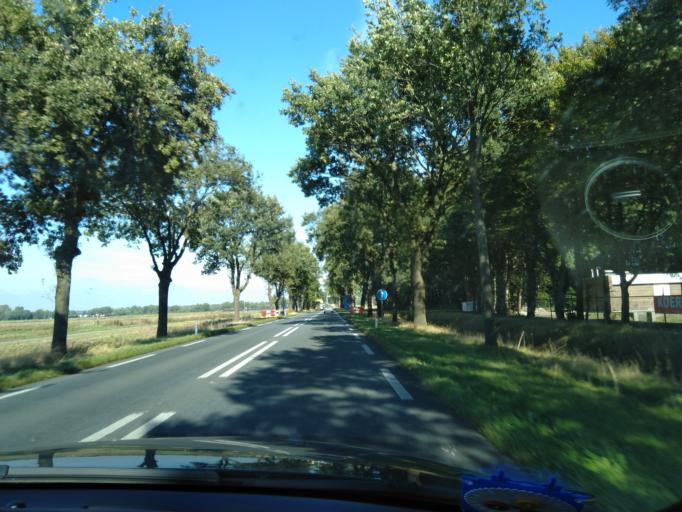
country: NL
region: Groningen
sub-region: Gemeente Pekela
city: Oude Pekela
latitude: 53.0963
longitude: 6.9802
